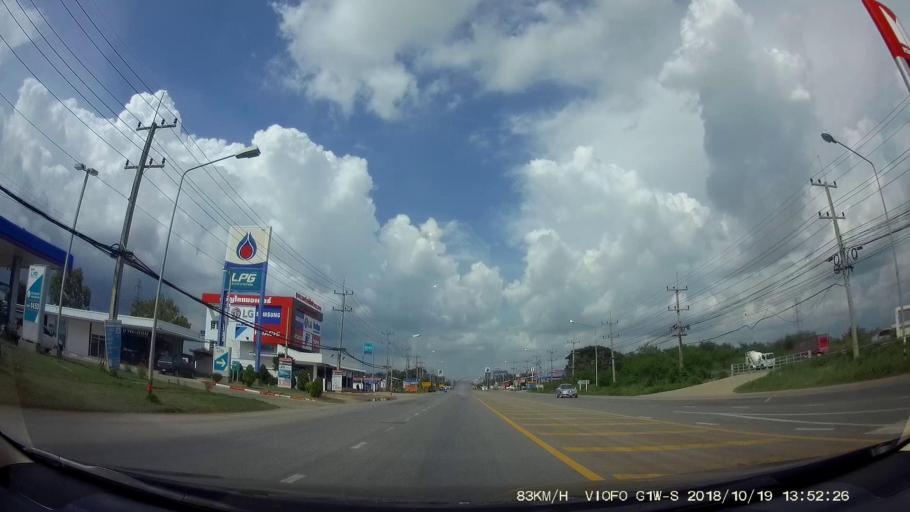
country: TH
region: Chaiyaphum
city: Chaiyaphum
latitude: 15.7670
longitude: 102.0252
